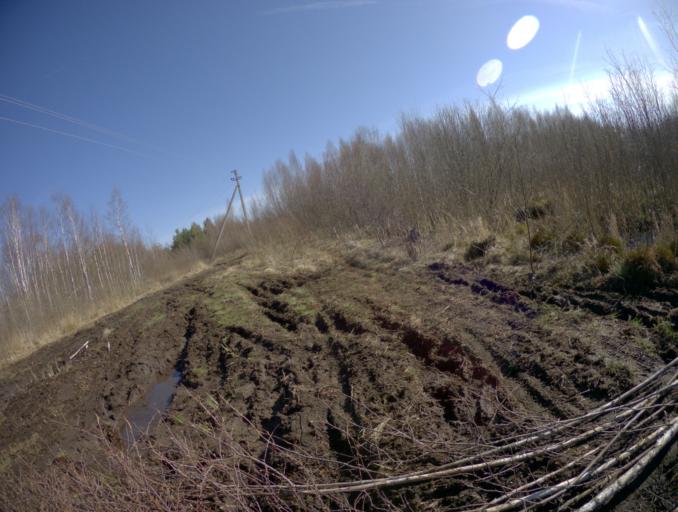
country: RU
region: Vladimir
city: Ivanishchi
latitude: 55.7365
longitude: 40.4087
